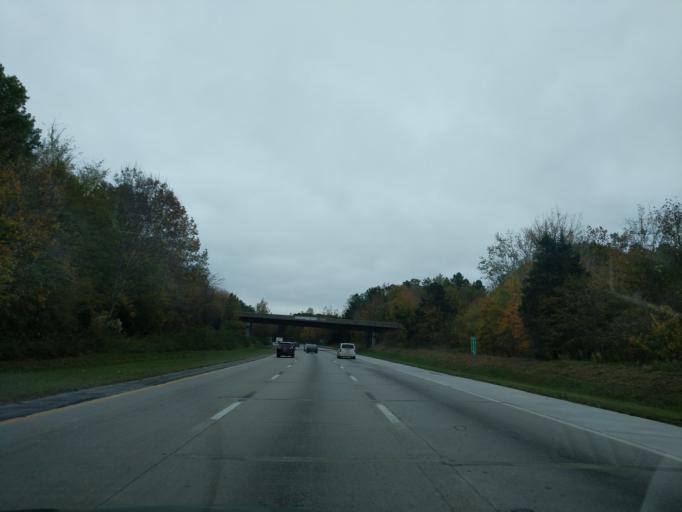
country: US
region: North Carolina
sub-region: Guilford County
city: Jamestown
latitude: 35.9407
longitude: -79.9046
